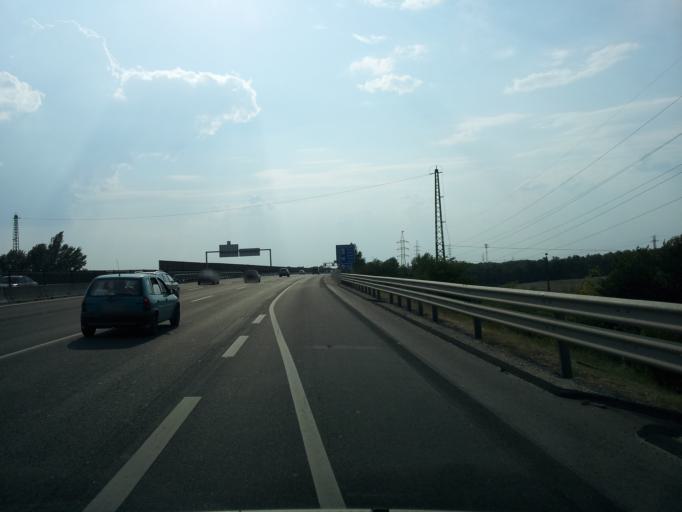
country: HU
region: Pest
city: Dunaharaszti
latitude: 47.3676
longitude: 19.1092
